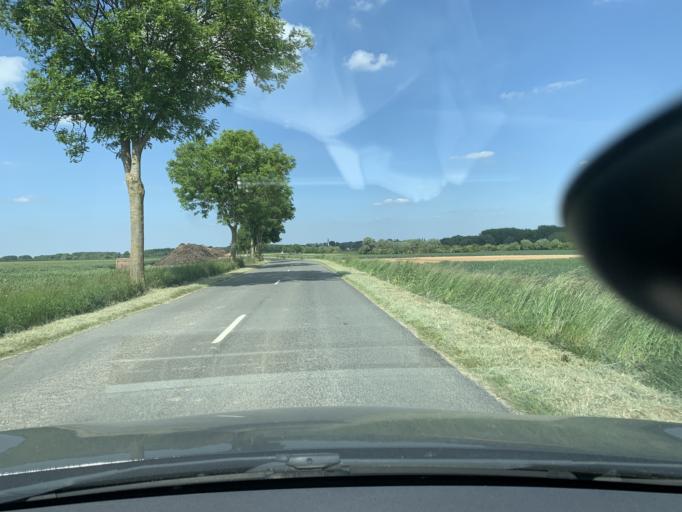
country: FR
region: Nord-Pas-de-Calais
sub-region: Departement du Pas-de-Calais
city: Marquion
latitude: 50.2269
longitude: 3.0821
